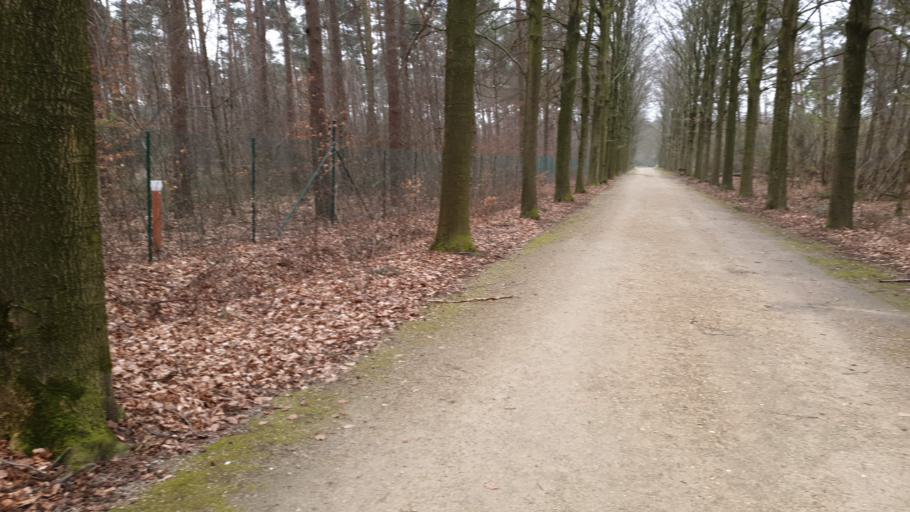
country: BE
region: Flanders
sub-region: Provincie Antwerpen
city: Brasschaat
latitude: 51.3081
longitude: 4.5188
